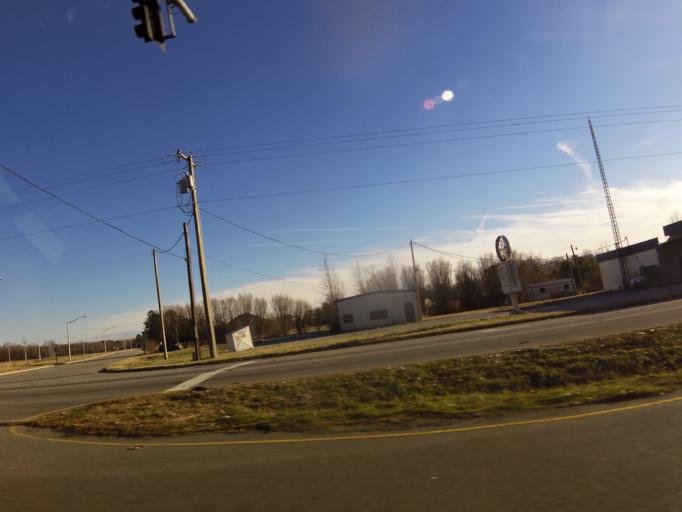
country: US
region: Virginia
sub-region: Isle of Wight County
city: Windsor
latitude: 36.6913
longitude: -76.7447
